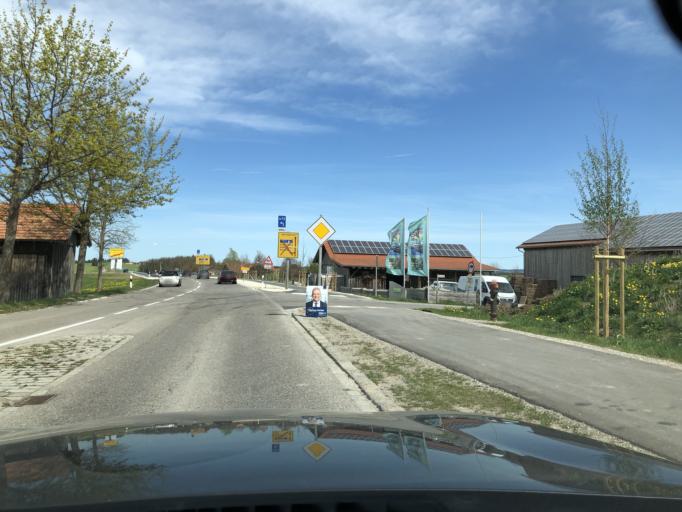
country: DE
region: Bavaria
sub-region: Swabia
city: Seeg
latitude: 47.6570
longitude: 10.6089
